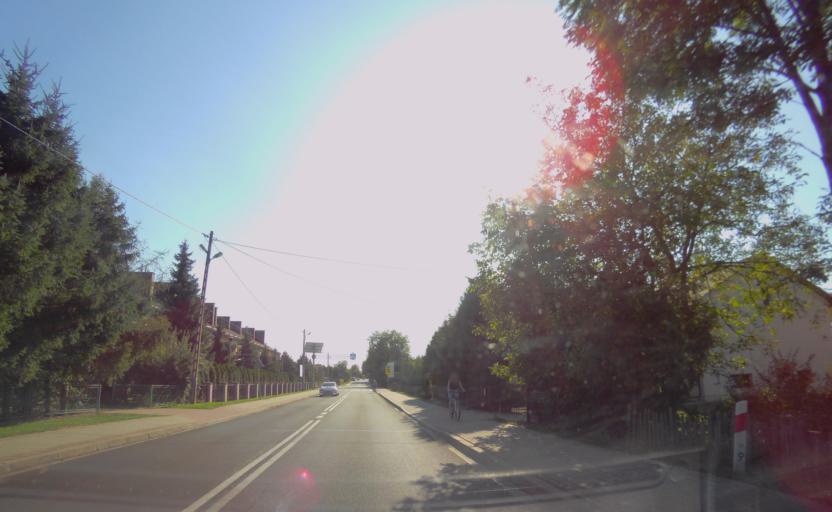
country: PL
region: Subcarpathian Voivodeship
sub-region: Powiat lezajski
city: Stare Miasto
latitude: 50.2910
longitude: 22.4318
